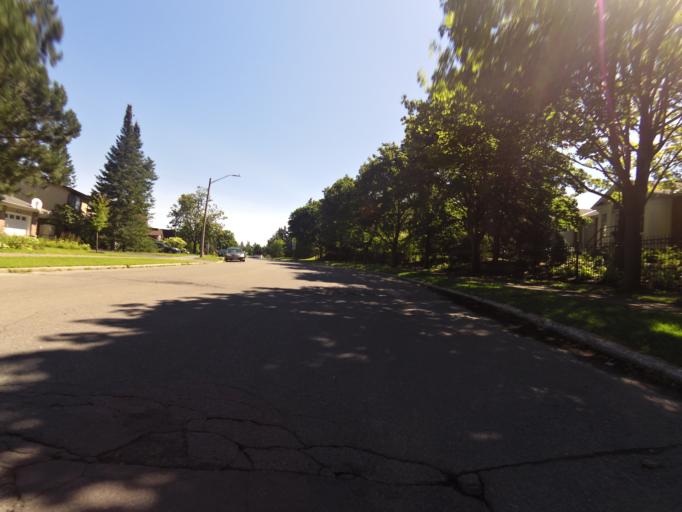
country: CA
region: Ontario
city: Ottawa
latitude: 45.3545
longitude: -75.6694
